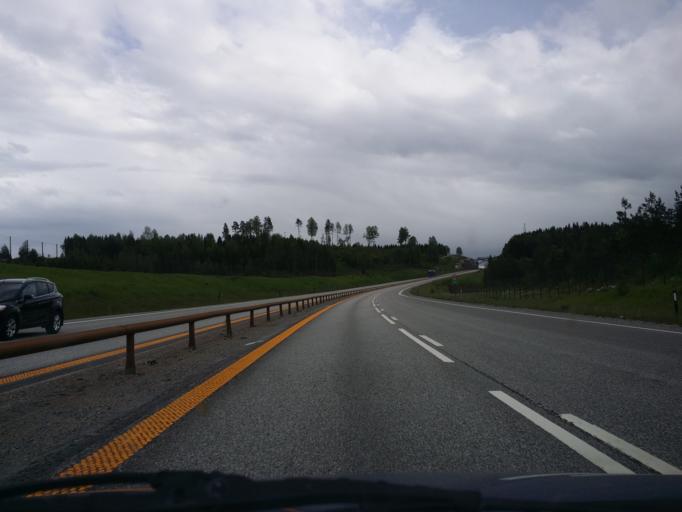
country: NO
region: Akershus
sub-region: Eidsvoll
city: Raholt
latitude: 60.2818
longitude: 11.1432
